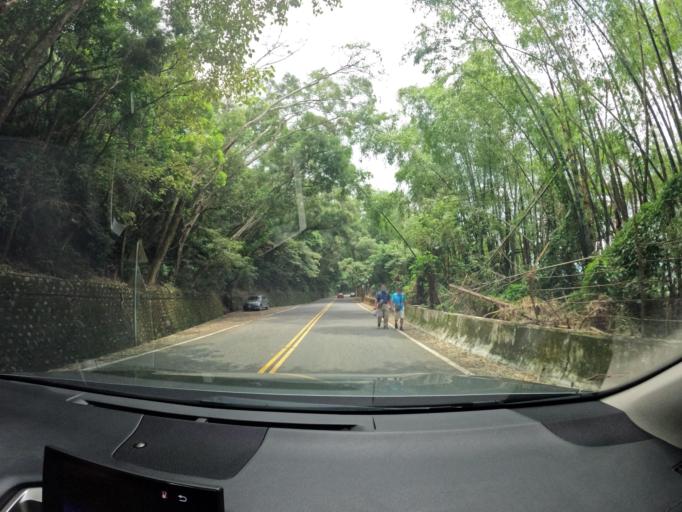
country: TW
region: Taiwan
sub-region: Nantou
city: Nantou
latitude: 23.8884
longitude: 120.6288
